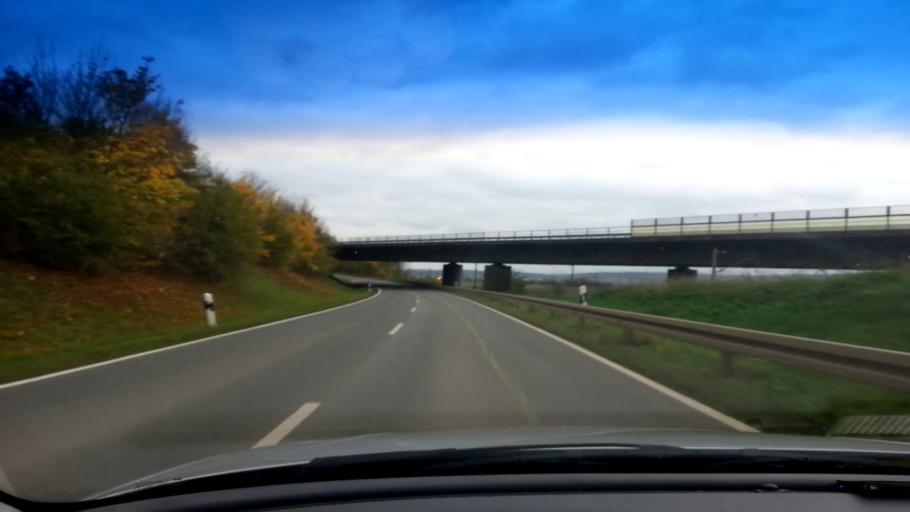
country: DE
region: Bavaria
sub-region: Regierungsbezirk Unterfranken
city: Stettfeld
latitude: 49.9617
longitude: 10.7311
